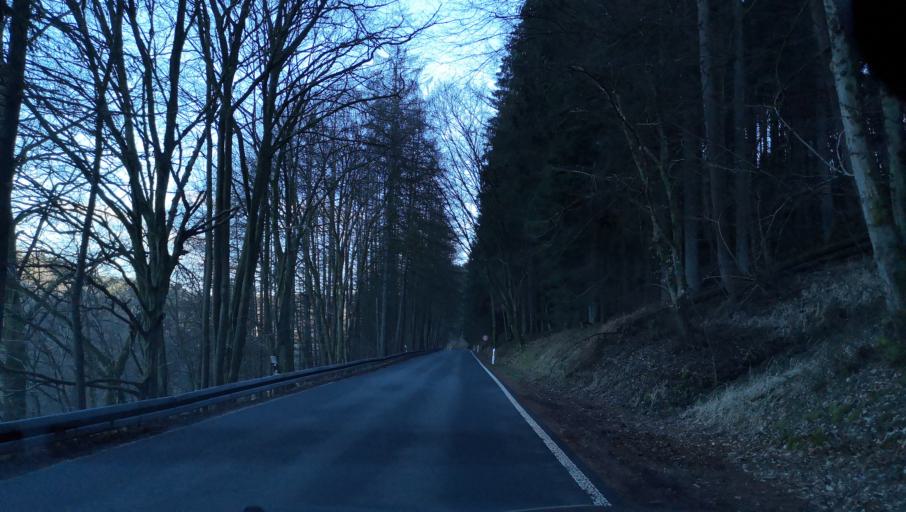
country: DE
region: North Rhine-Westphalia
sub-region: Regierungsbezirk Arnsberg
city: Breckerfeld
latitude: 51.2626
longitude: 7.4148
